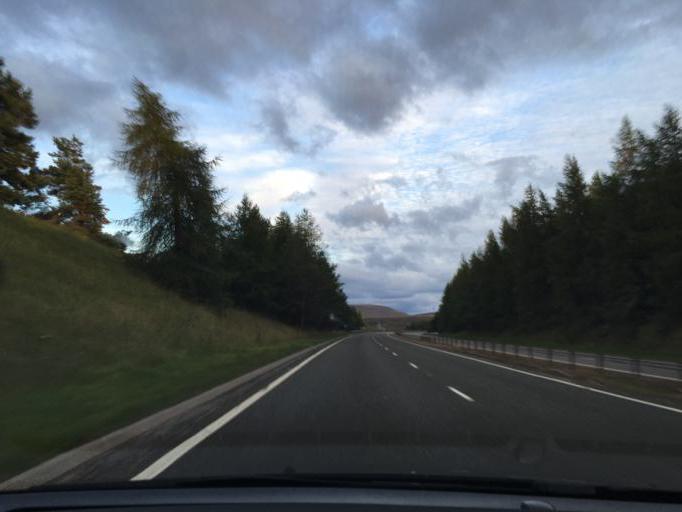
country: GB
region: Scotland
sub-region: Highland
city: Aviemore
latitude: 57.3386
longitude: -3.9857
